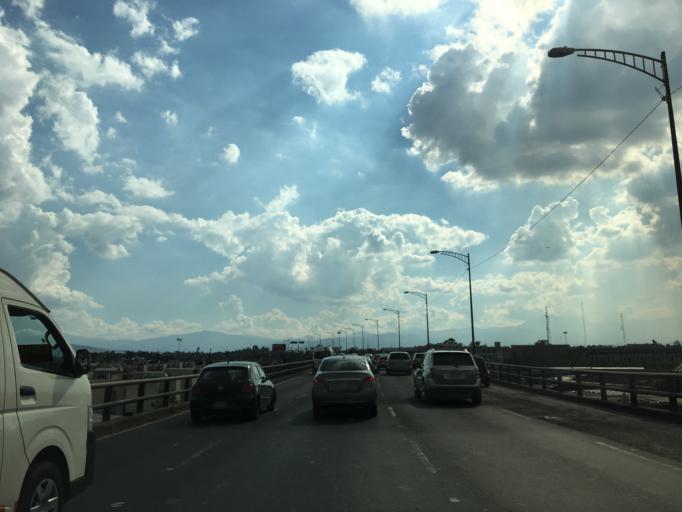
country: MX
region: Mexico City
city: Venustiano Carranza
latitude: 19.4318
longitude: -99.1104
